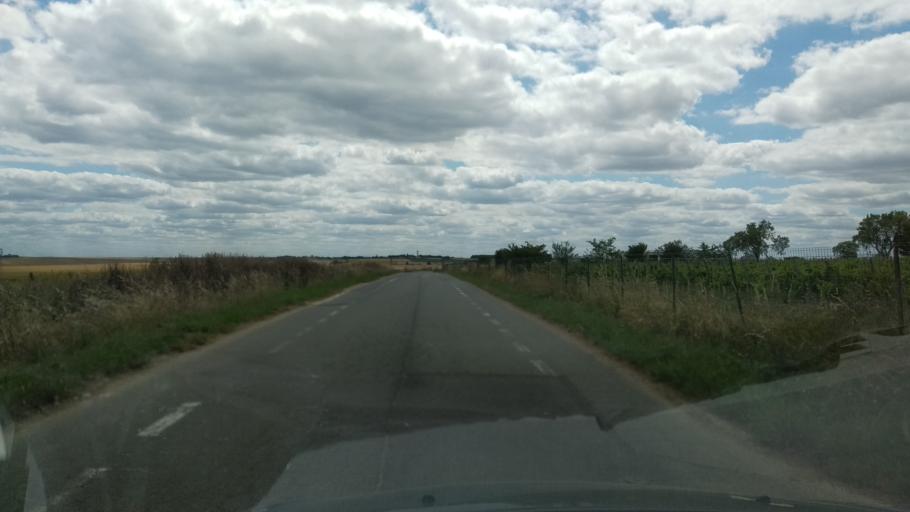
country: FR
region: Poitou-Charentes
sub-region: Departement de la Vienne
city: Jaunay-Clan
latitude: 46.6805
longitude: 0.3553
